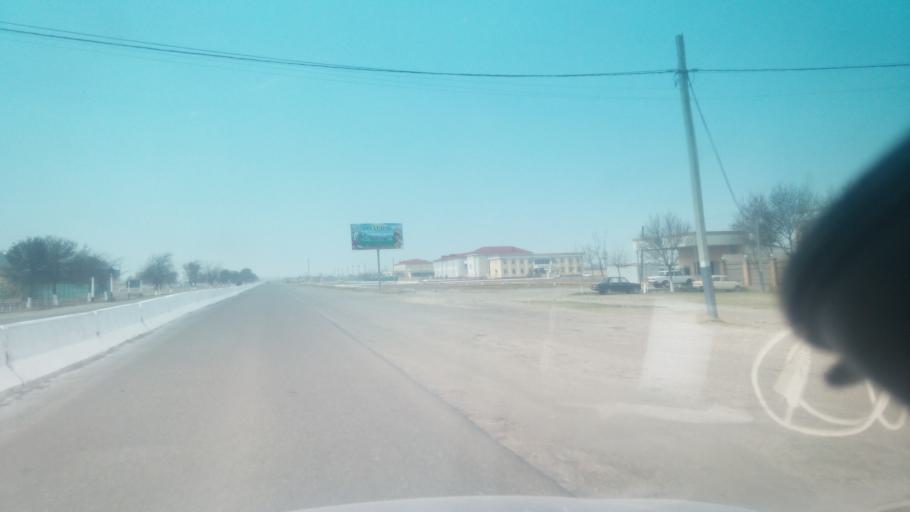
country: UZ
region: Sirdaryo
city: Yangiyer
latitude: 40.2290
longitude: 68.8375
